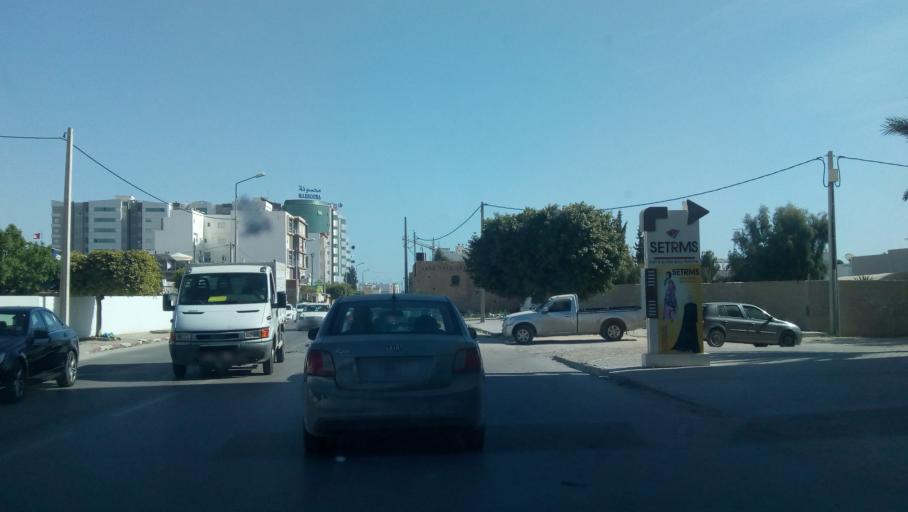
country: TN
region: Safaqis
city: Sfax
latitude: 34.7645
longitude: 10.7260
